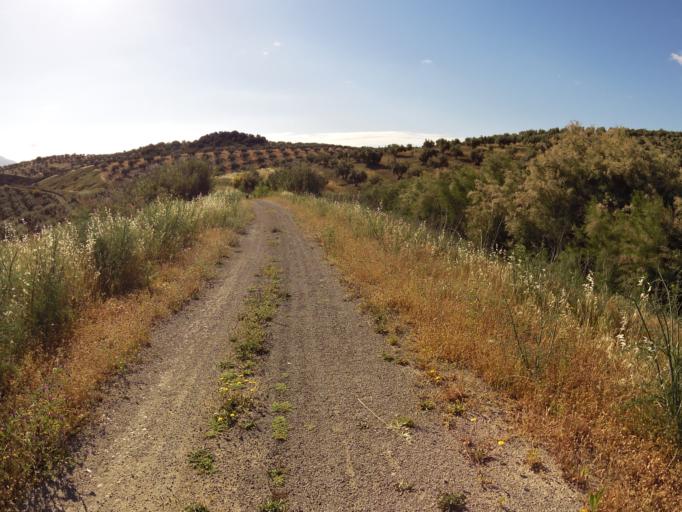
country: ES
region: Andalusia
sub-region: Province of Cordoba
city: Fuente-Tojar
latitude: 37.5788
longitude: -4.1833
